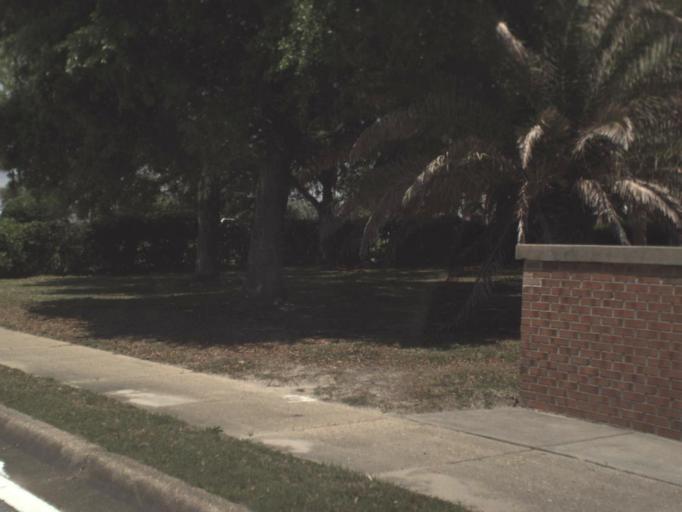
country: US
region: Florida
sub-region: Escambia County
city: East Pensacola Heights
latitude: 30.4182
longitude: -87.1964
